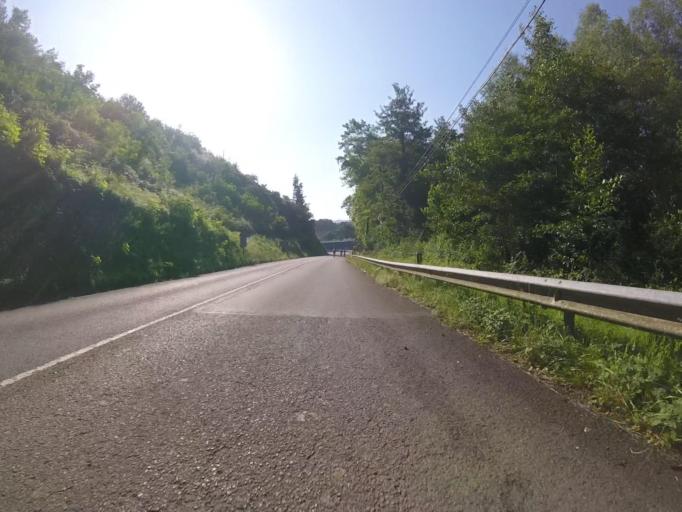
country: ES
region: Basque Country
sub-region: Provincia de Guipuzcoa
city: Asteasu
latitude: 43.1907
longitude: -2.0882
